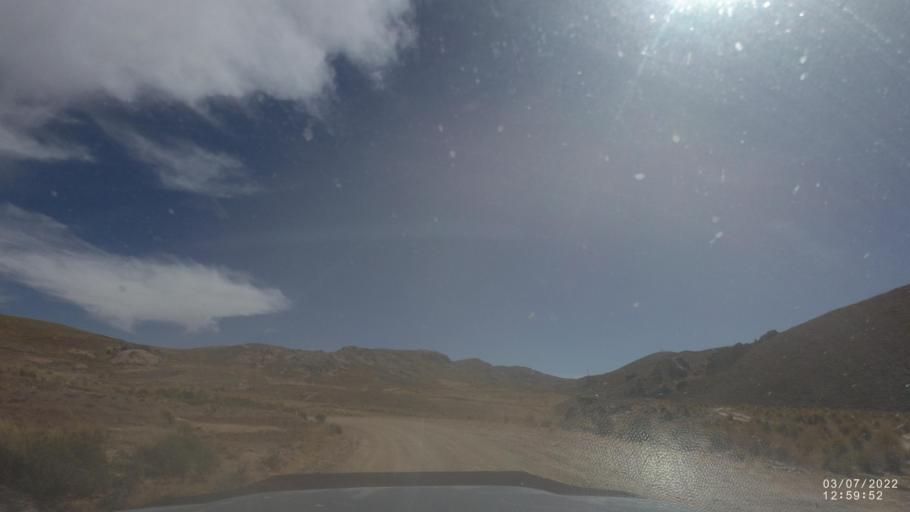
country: BO
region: Cochabamba
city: Colchani
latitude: -17.7148
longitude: -66.6864
